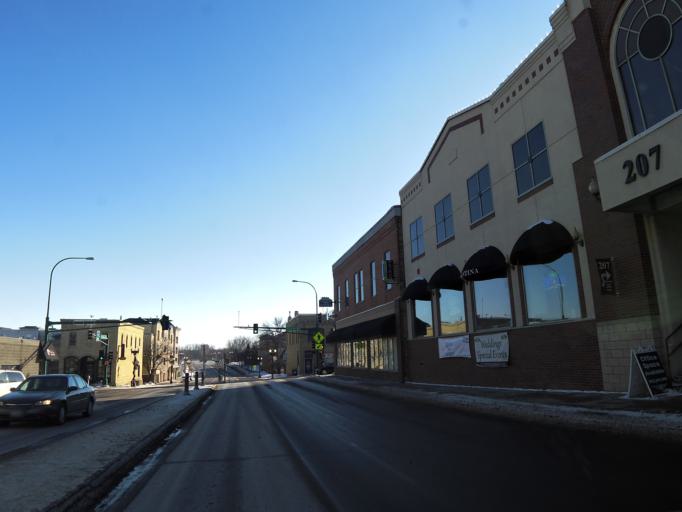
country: US
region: Minnesota
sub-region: Carver County
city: Chaska
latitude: 44.7858
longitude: -93.6006
